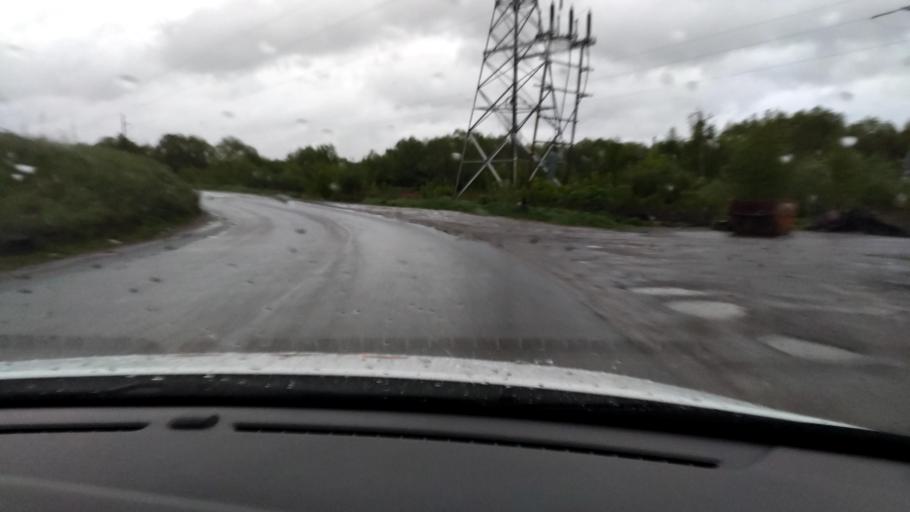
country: RU
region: Tatarstan
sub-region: Gorod Kazan'
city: Kazan
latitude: 55.7217
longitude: 49.1178
